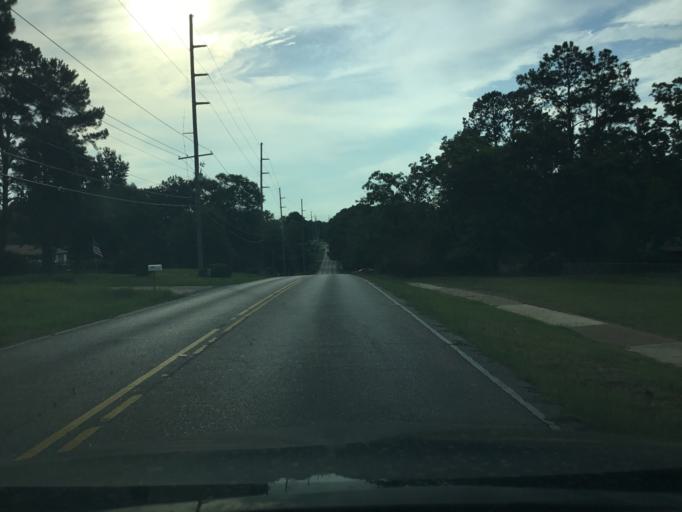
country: US
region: Alabama
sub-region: Montgomery County
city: Montgomery
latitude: 32.3671
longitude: -86.2501
